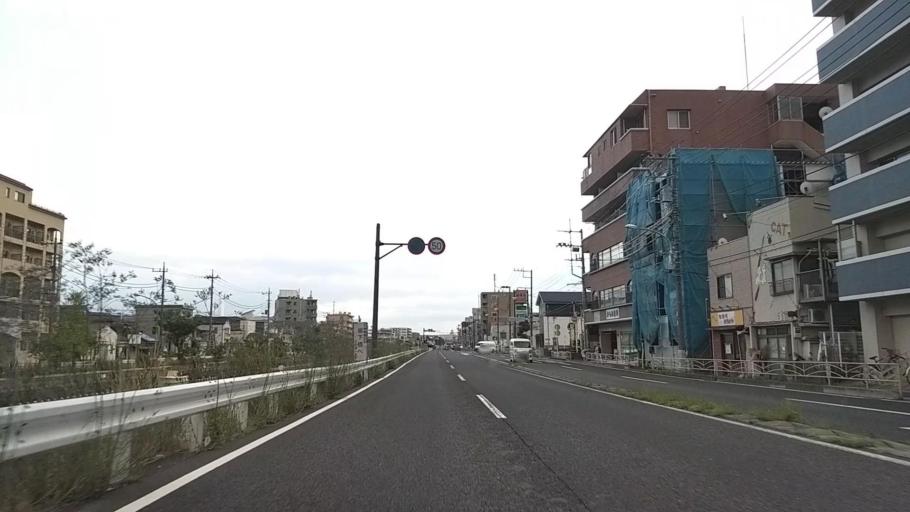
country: JP
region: Kanagawa
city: Yokohama
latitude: 35.4248
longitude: 139.6237
